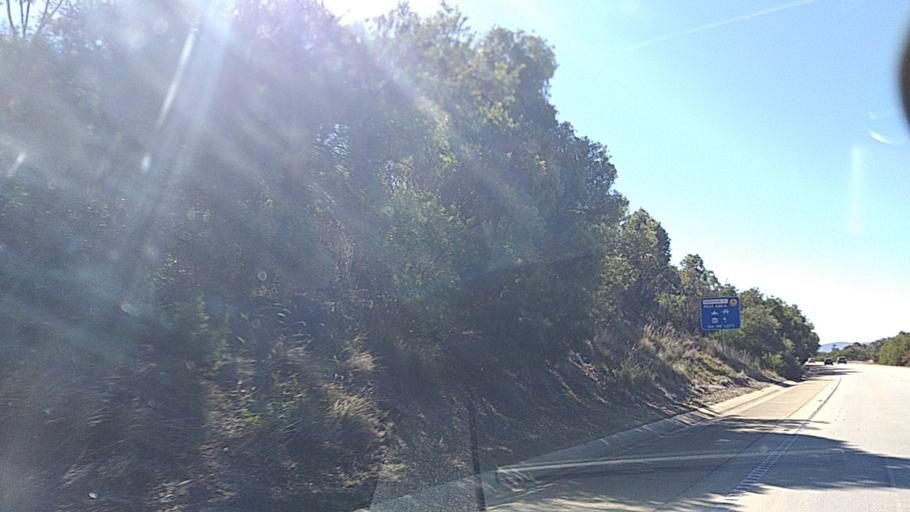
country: AU
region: New South Wales
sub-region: Yass Valley
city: Gundaroo
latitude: -35.1095
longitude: 149.3685
